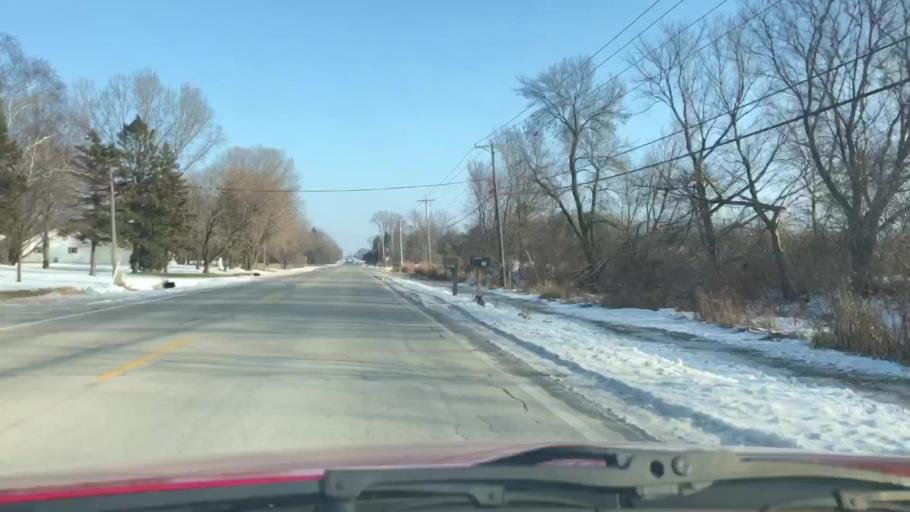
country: US
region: Wisconsin
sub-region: Outagamie County
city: Appleton
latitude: 44.3167
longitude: -88.4268
